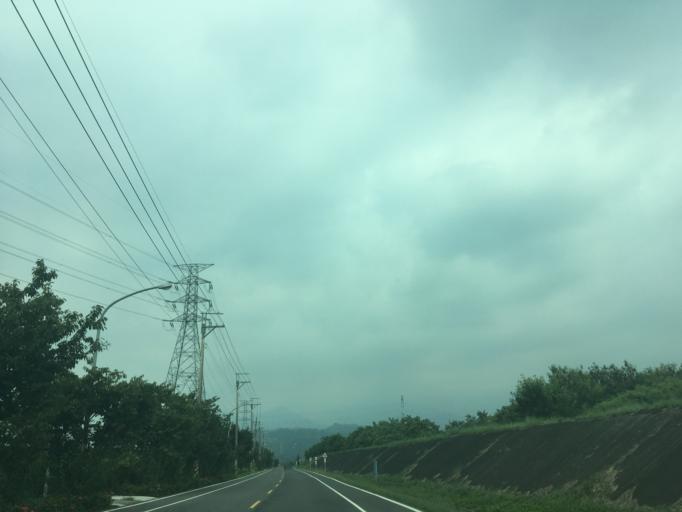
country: TW
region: Taiwan
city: Fengyuan
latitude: 24.2904
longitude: 120.8442
